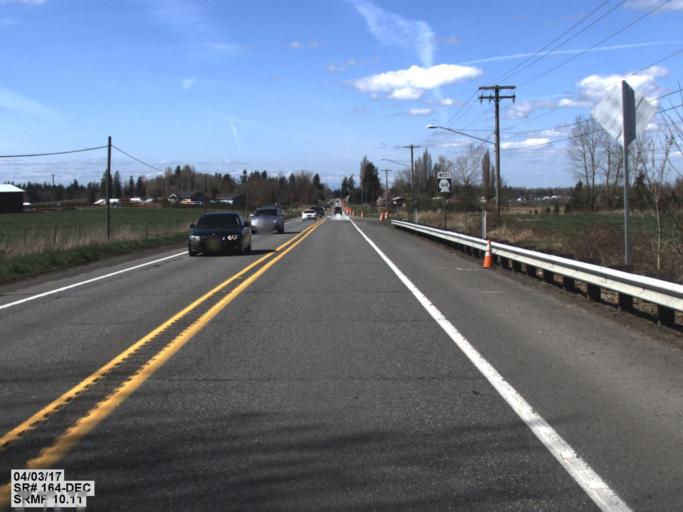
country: US
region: Washington
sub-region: Pierce County
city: Buckley
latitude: 47.2119
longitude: -122.0821
